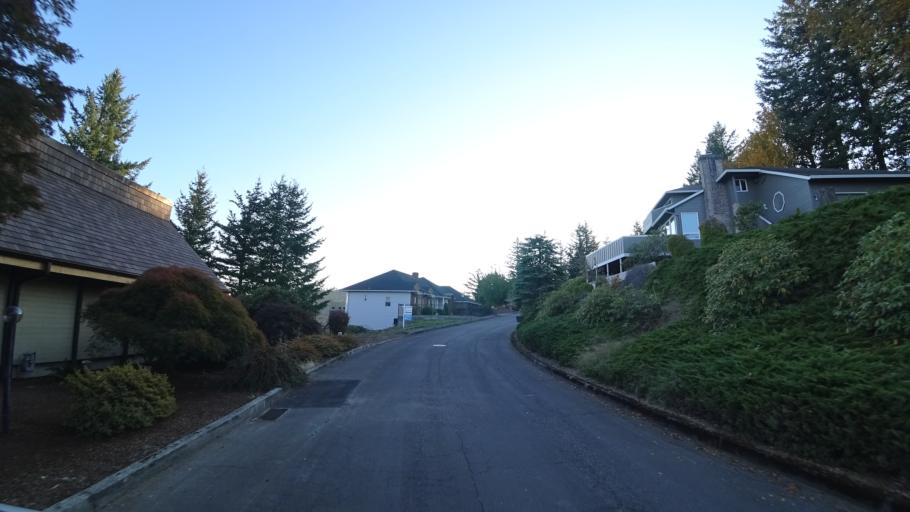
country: US
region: Oregon
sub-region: Multnomah County
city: Gresham
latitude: 45.4860
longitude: -122.4329
